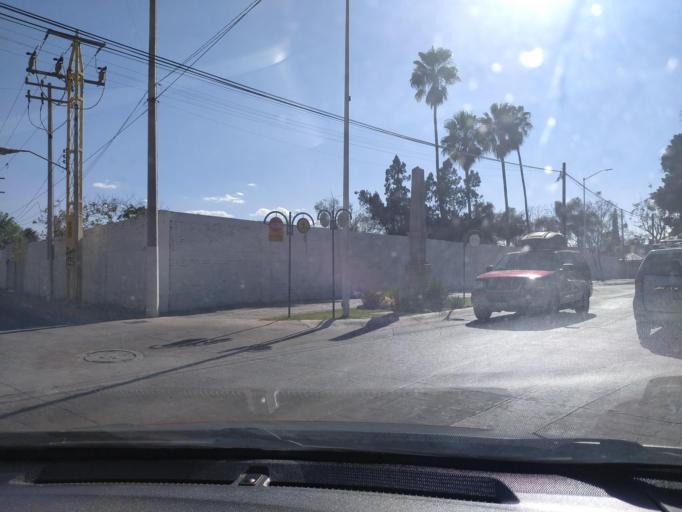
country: LA
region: Oudomxai
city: Muang La
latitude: 21.0247
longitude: 101.8400
